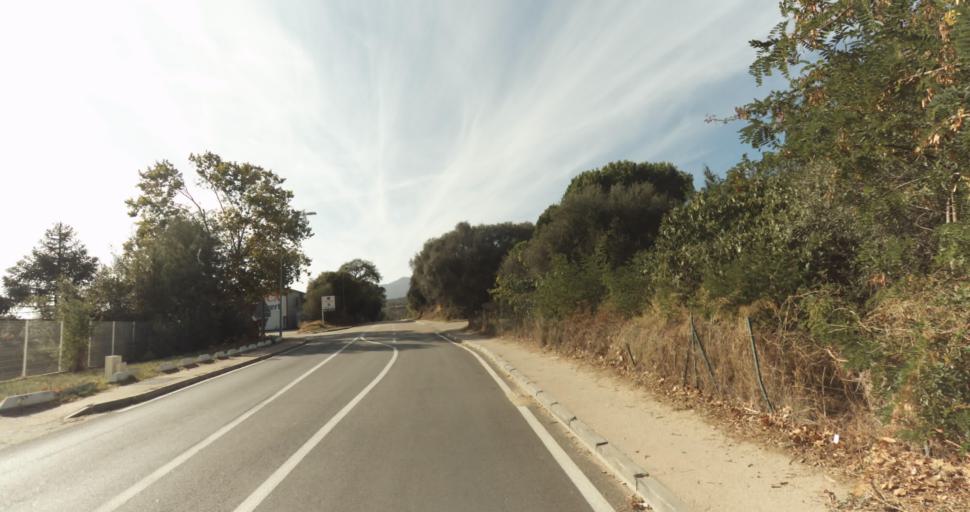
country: FR
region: Corsica
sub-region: Departement de la Corse-du-Sud
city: Afa
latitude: 41.9283
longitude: 8.7944
